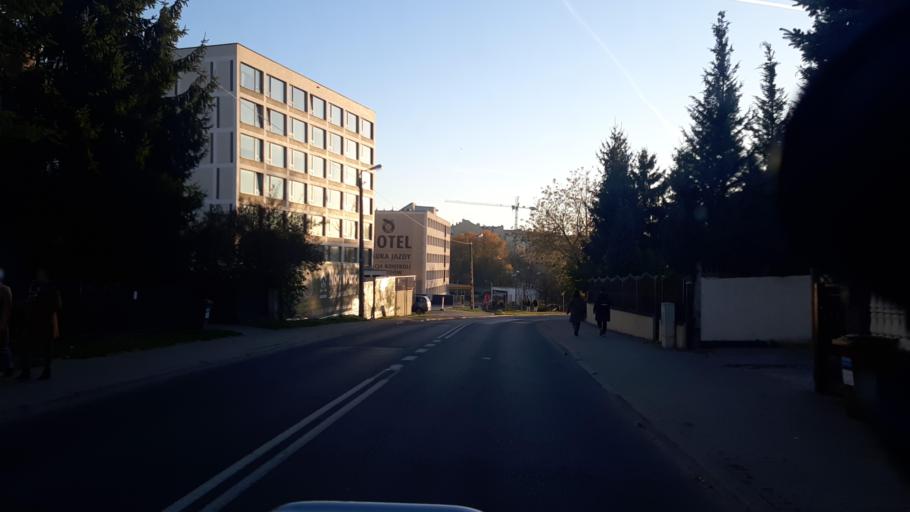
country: PL
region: Lublin Voivodeship
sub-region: Powiat lubelski
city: Lublin
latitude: 51.2550
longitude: 22.5634
